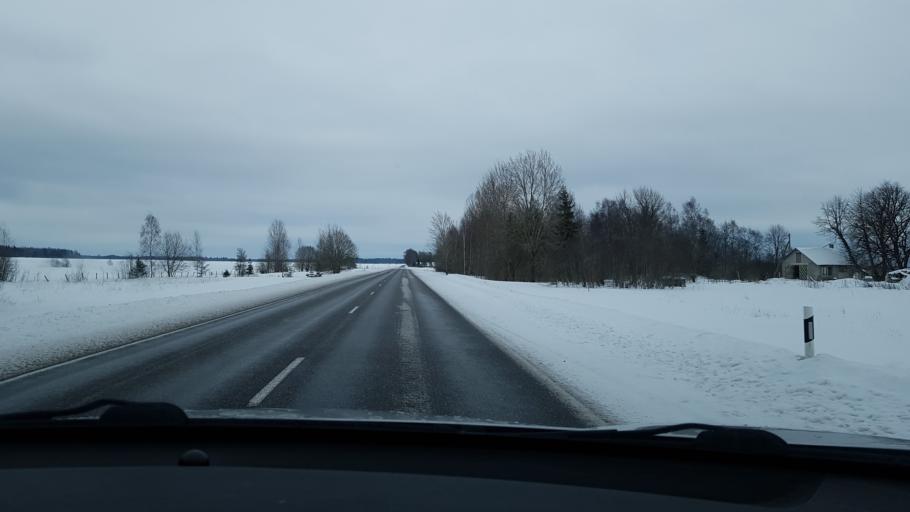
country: EE
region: Jaervamaa
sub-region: Jaerva-Jaani vald
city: Jarva-Jaani
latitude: 59.1275
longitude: 25.7821
